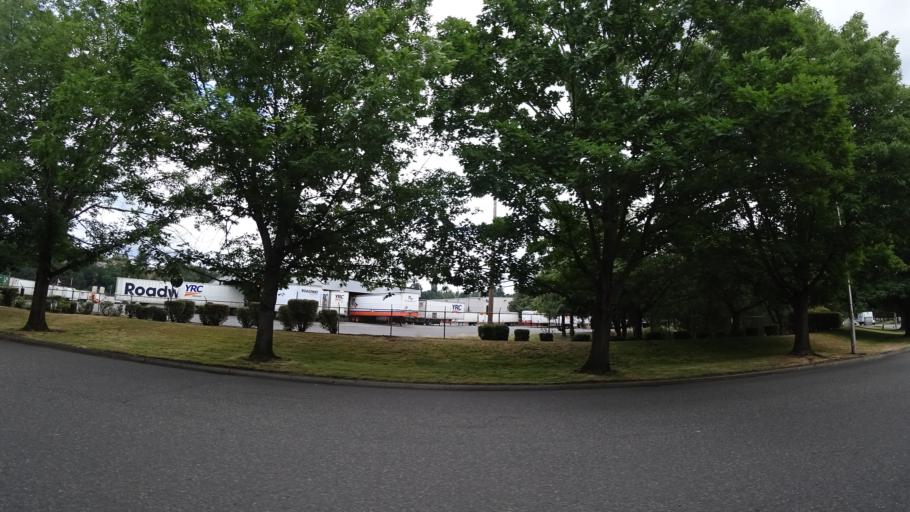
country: US
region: Oregon
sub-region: Multnomah County
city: Portland
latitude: 45.5709
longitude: -122.7088
